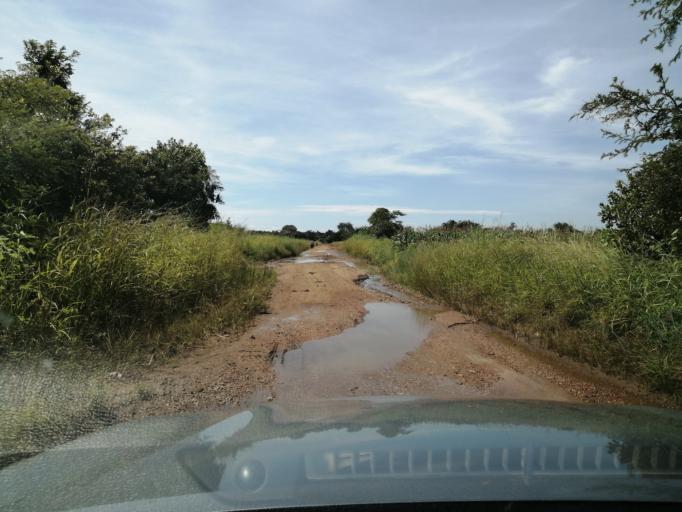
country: ZM
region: Central
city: Chibombo
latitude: -14.9977
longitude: 27.8184
